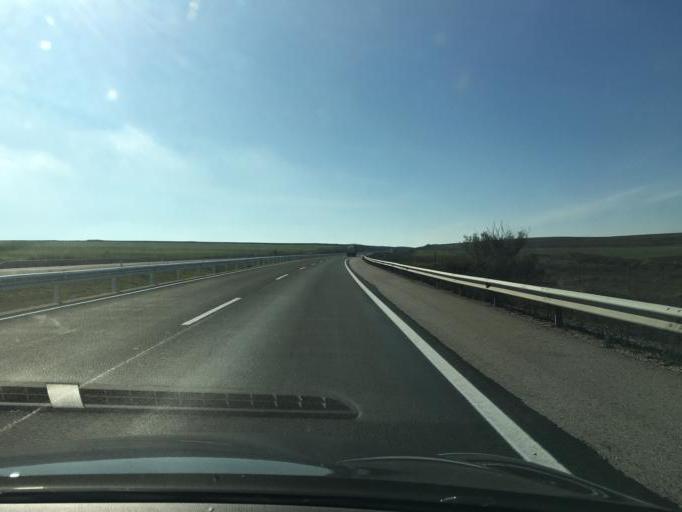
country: ES
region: Castille and Leon
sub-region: Provincia de Burgos
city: Zuneda
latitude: 42.5938
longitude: -3.2292
